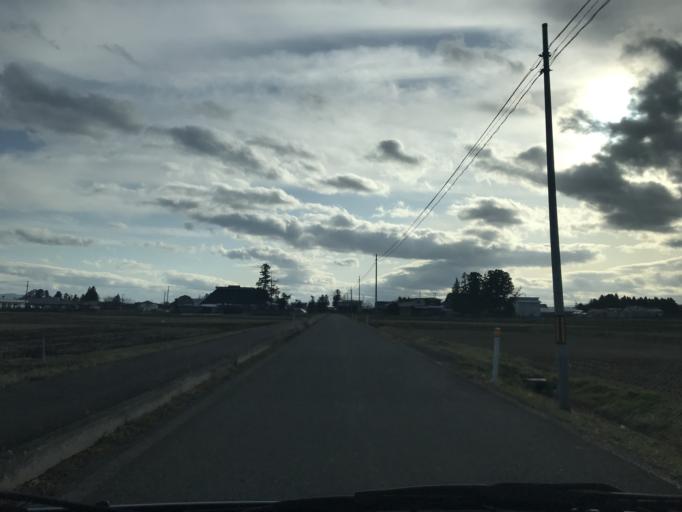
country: JP
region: Iwate
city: Mizusawa
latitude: 39.1893
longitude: 141.1034
